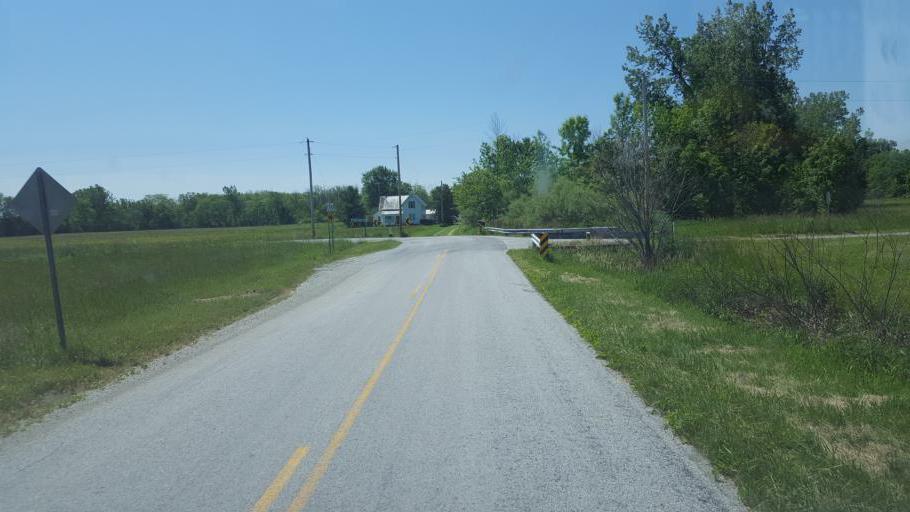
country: US
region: Ohio
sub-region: Hardin County
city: Kenton
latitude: 40.6078
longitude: -83.4203
